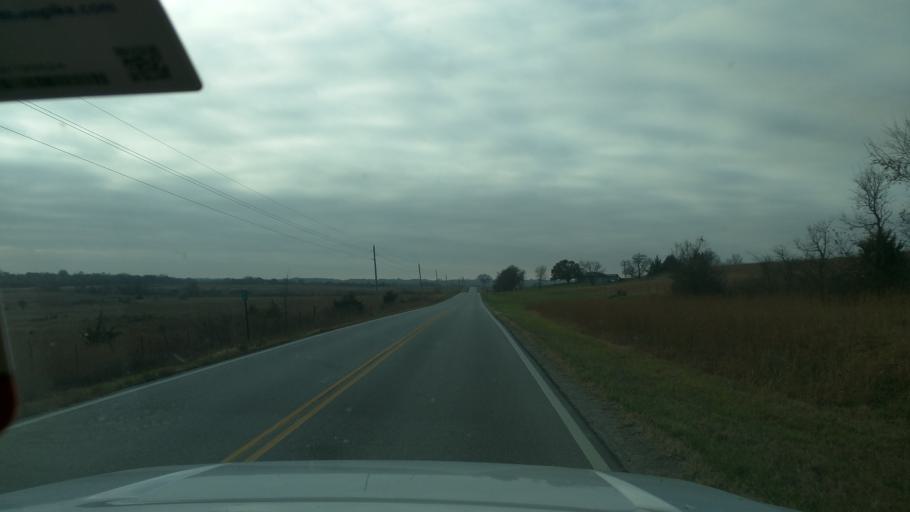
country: US
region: Kansas
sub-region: Greenwood County
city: Eureka
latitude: 37.7305
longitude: -96.2298
